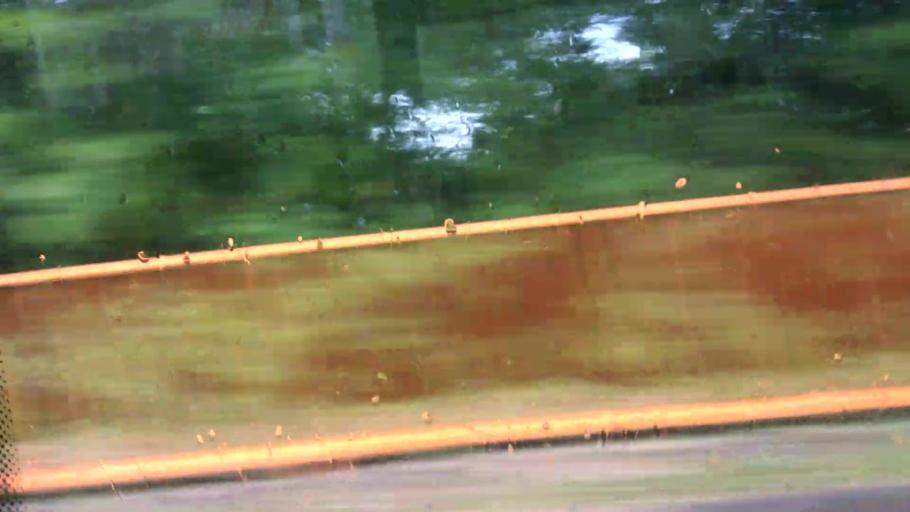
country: RU
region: Moskovskaya
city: Zaraysk
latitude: 54.7560
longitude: 38.8731
